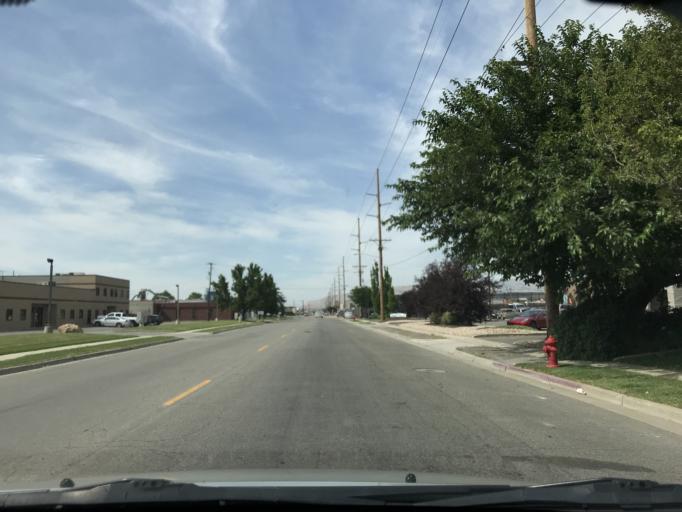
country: US
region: Utah
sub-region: Salt Lake County
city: Centerfield
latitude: 40.6908
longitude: -111.9055
